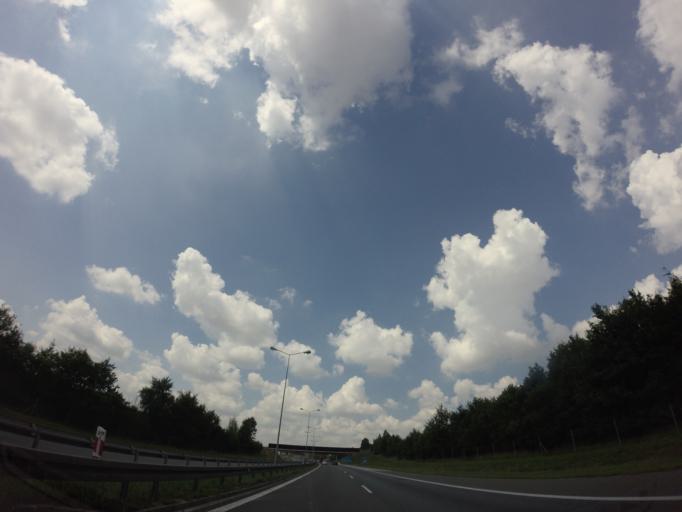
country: PL
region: Opole Voivodeship
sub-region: Powiat strzelecki
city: Ujazd
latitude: 50.4437
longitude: 18.3548
